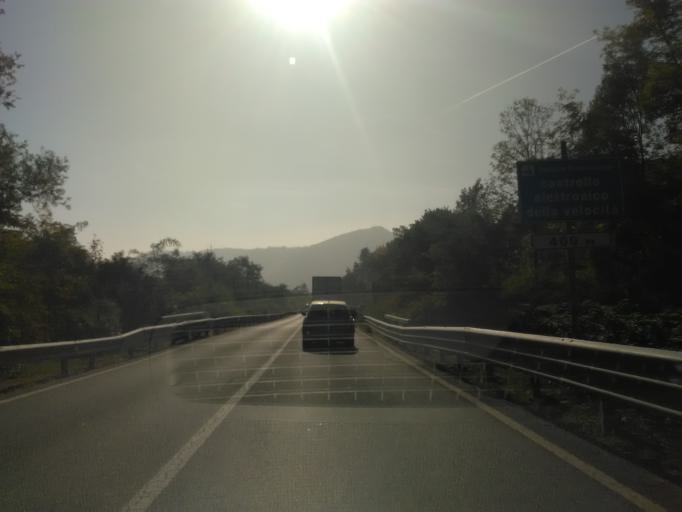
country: IT
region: Piedmont
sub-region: Provincia di Vercelli
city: Borgosesia
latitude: 45.7287
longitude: 8.2611
